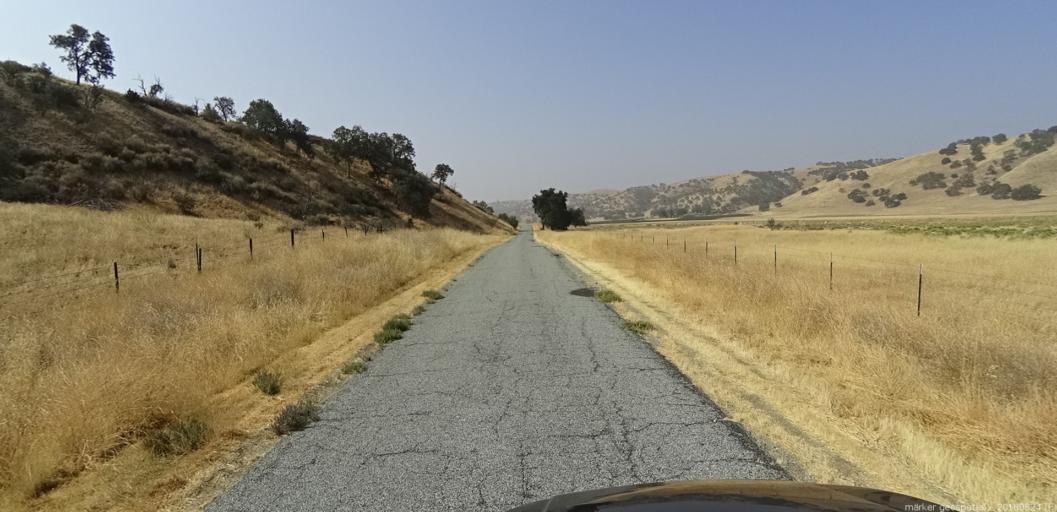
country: US
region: California
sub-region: San Luis Obispo County
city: San Miguel
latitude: 35.9017
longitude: -120.6958
